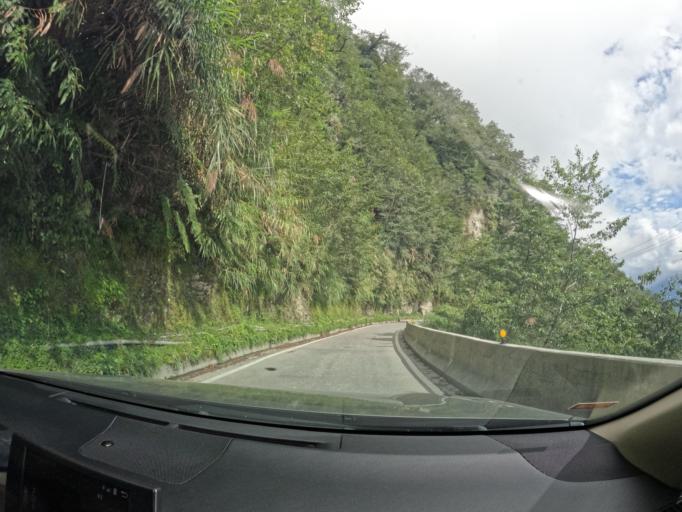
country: TW
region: Taiwan
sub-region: Taitung
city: Taitung
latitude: 23.2376
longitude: 121.0048
